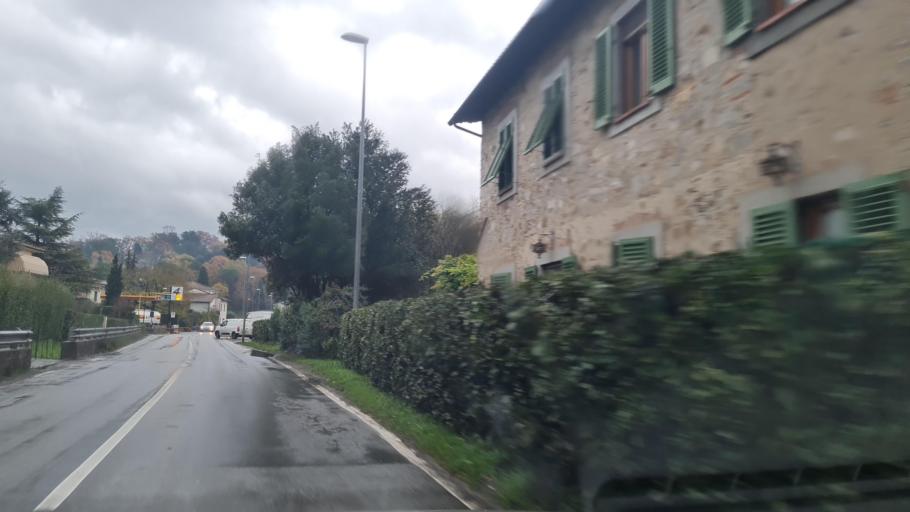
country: IT
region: Tuscany
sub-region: Provincia di Lucca
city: Lucca
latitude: 43.8614
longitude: 10.4867
